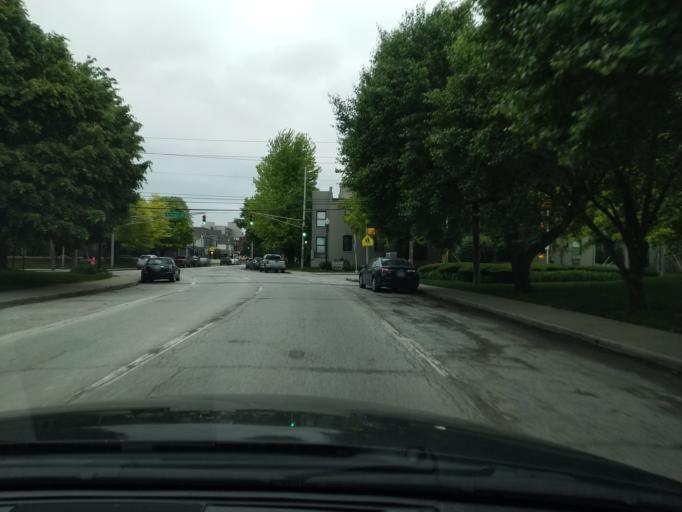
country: US
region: Indiana
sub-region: Marion County
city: Indianapolis
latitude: 39.7782
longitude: -86.1488
